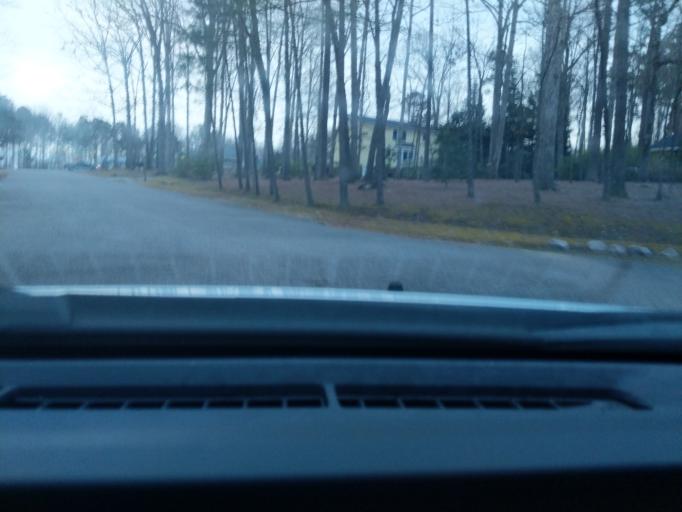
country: US
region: North Carolina
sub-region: Wake County
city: Garner
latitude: 35.7153
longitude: -78.6868
